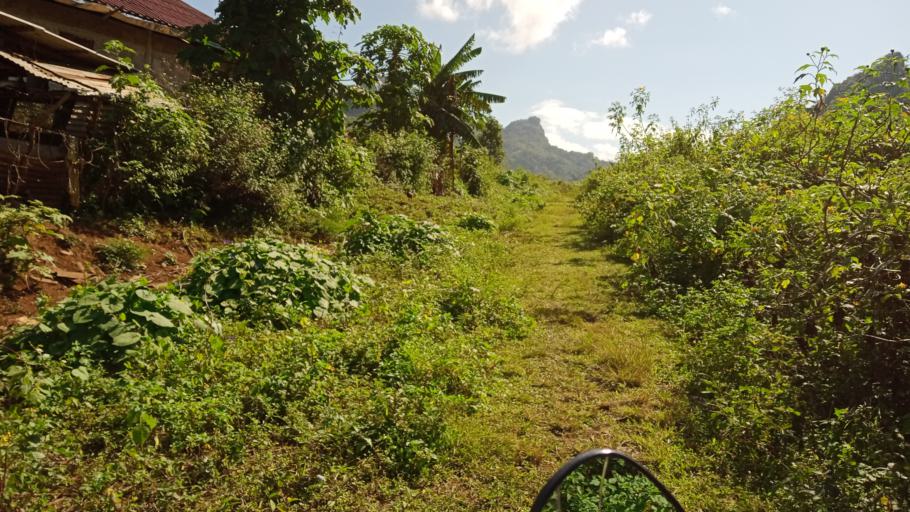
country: LA
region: Xiangkhoang
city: Phonsavan
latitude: 19.1037
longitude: 102.9328
